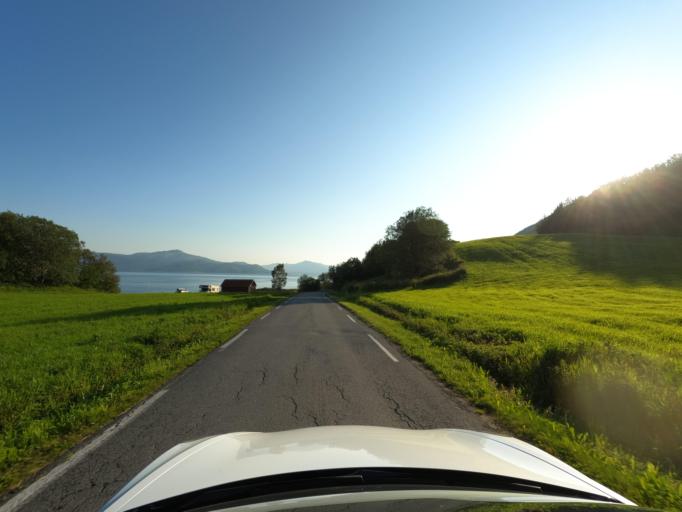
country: NO
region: Nordland
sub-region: Ballangen
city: Ballangen
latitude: 68.4705
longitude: 16.8667
